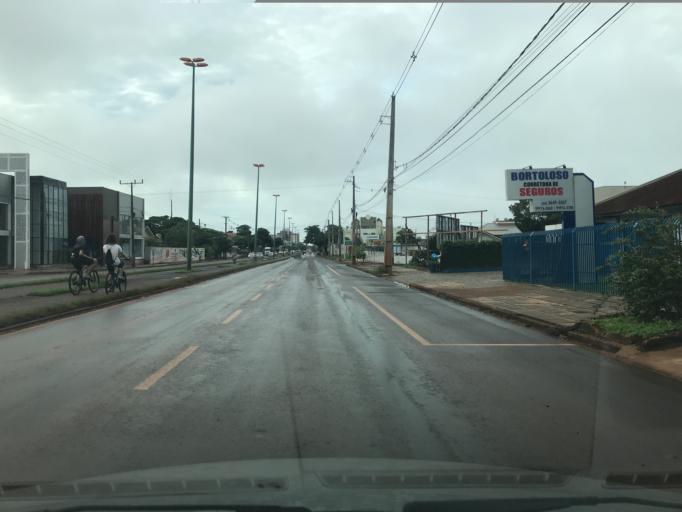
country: BR
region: Parana
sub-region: Palotina
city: Palotina
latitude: -24.2929
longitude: -53.8368
